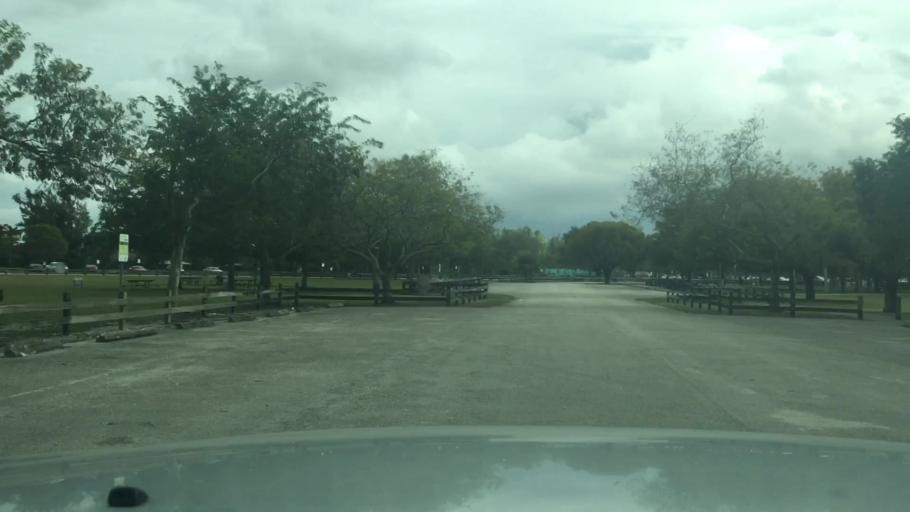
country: US
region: Florida
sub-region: Miami-Dade County
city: Opa-locka
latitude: 25.8865
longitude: -80.2747
